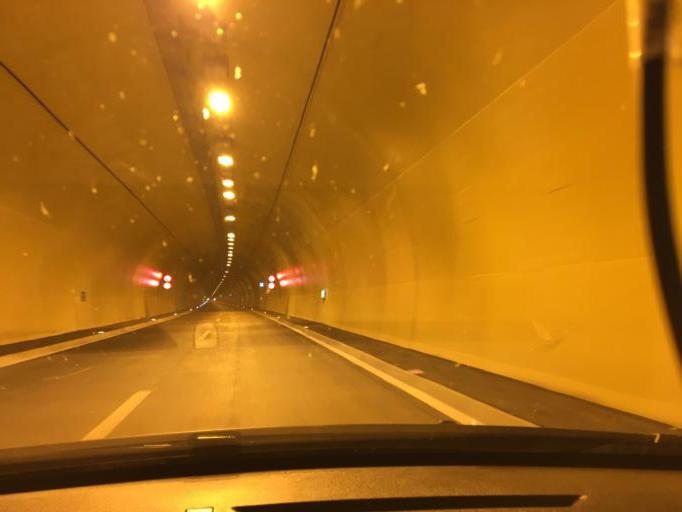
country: MK
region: Demir Kapija
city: Demir Kapija
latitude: 41.4089
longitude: 22.2530
